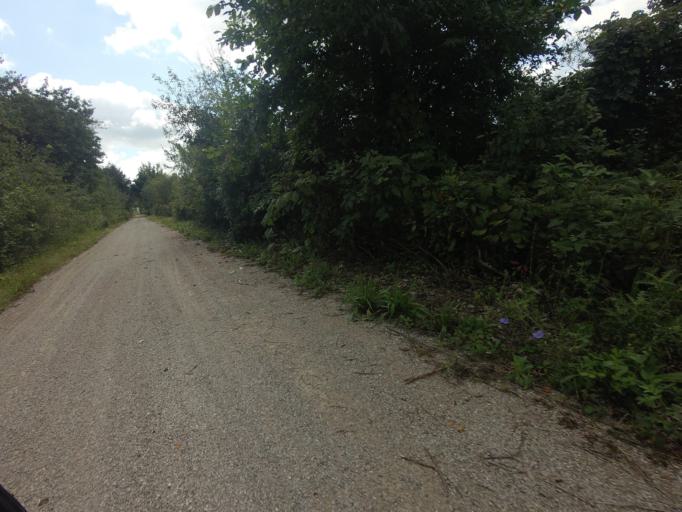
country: CA
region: Ontario
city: Huron East
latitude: 43.6557
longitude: -81.2400
